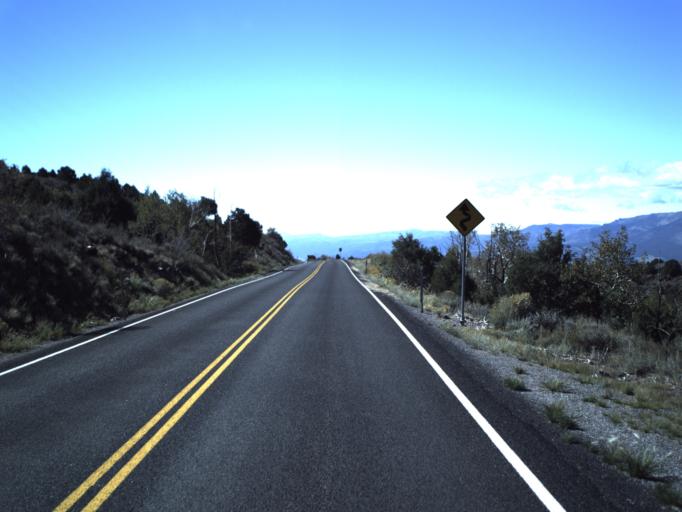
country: US
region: Utah
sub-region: Wayne County
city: Loa
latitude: 38.4847
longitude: -111.8223
